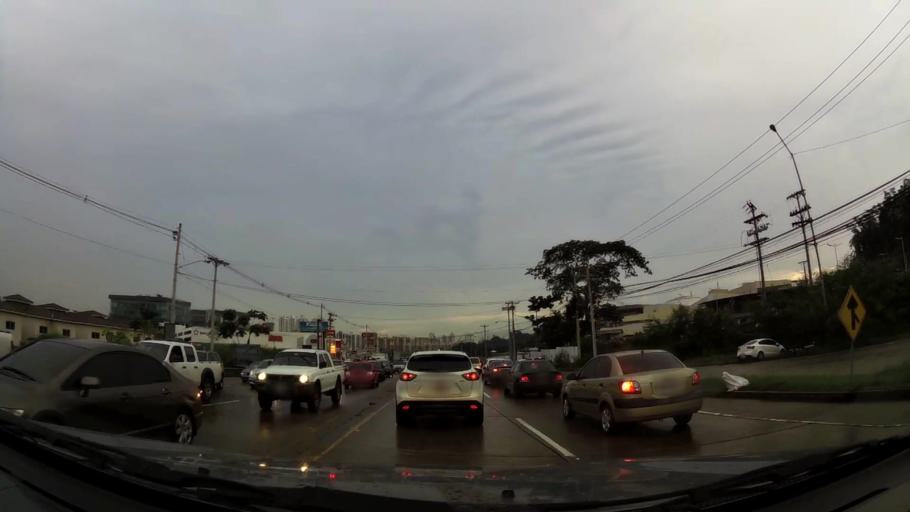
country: PA
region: Panama
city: Panama
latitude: 9.0324
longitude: -79.5353
